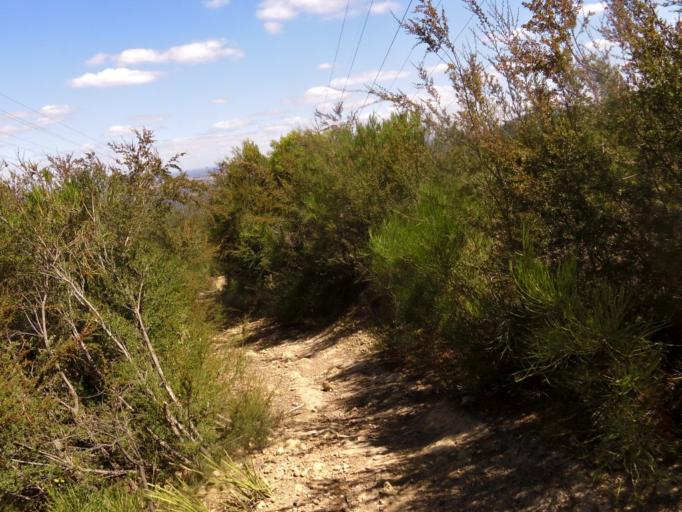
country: AU
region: Victoria
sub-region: Nillumbik
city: Saint Andrews
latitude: -37.5218
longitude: 145.3052
